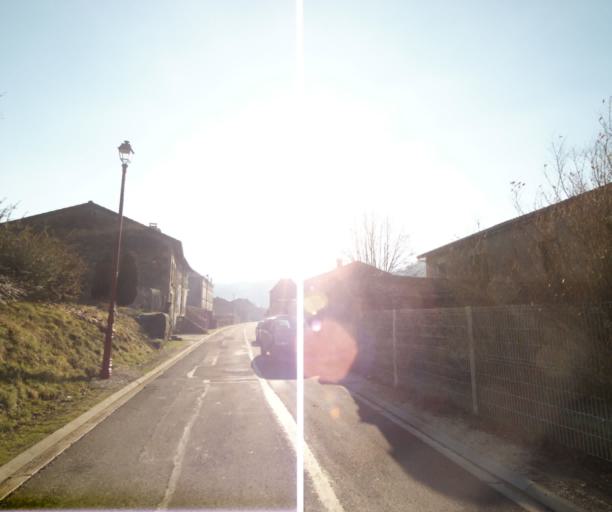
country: FR
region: Champagne-Ardenne
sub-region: Departement de la Haute-Marne
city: Chevillon
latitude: 48.4974
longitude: 5.1927
